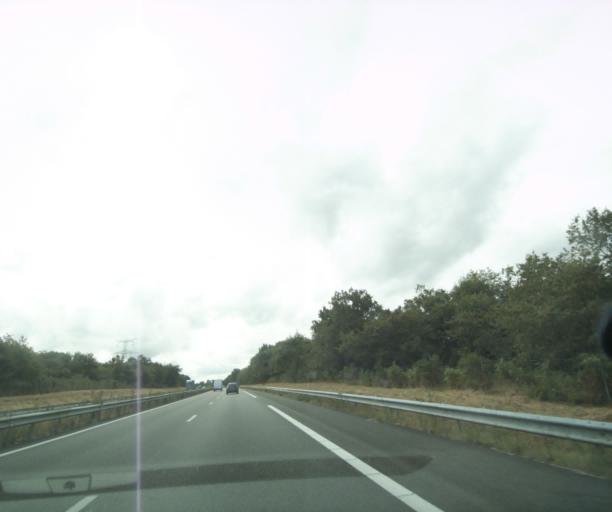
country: FR
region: Poitou-Charentes
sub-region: Departement de la Charente-Maritime
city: Saint-Genis-de-Saintonge
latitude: 45.4637
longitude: -0.6198
